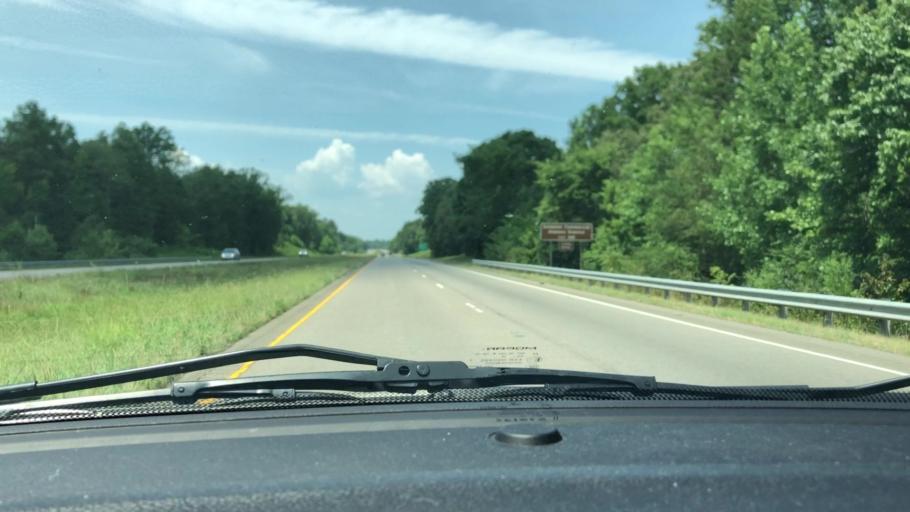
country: US
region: North Carolina
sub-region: Chatham County
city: Farmville
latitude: 35.5838
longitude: -79.3125
